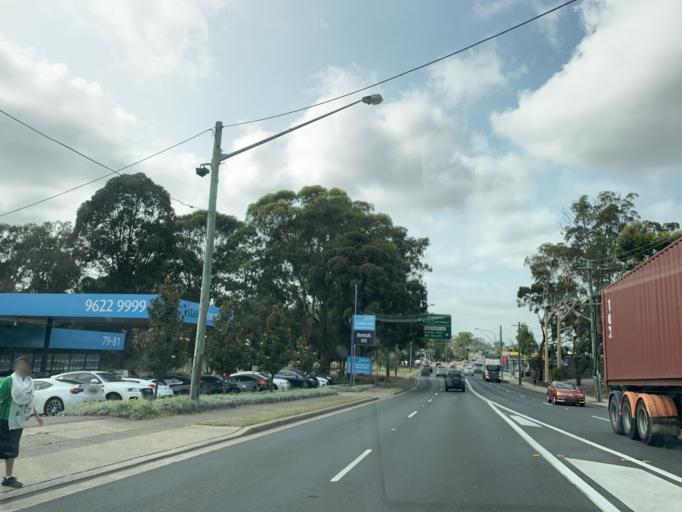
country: AU
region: New South Wales
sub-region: Blacktown
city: Blacktown
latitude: -33.7778
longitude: 150.9202
